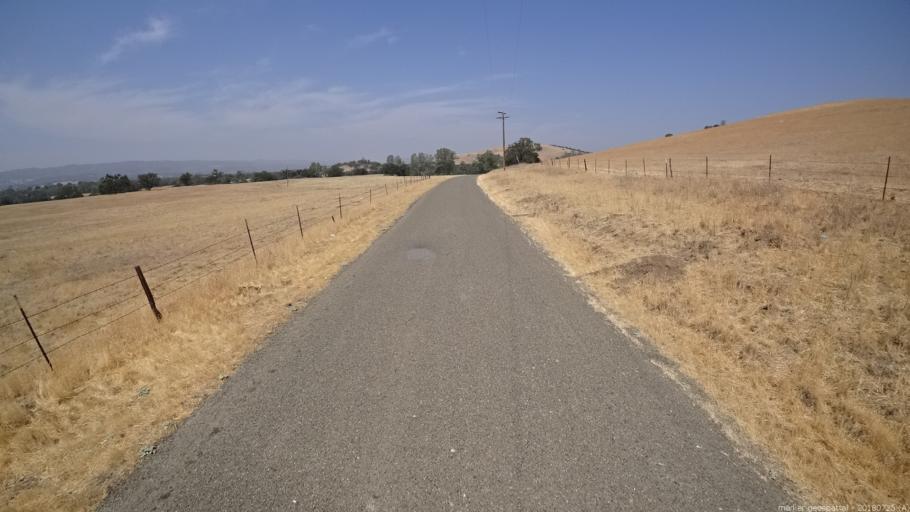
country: US
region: California
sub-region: San Luis Obispo County
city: Shandon
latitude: 35.8775
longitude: -120.3923
